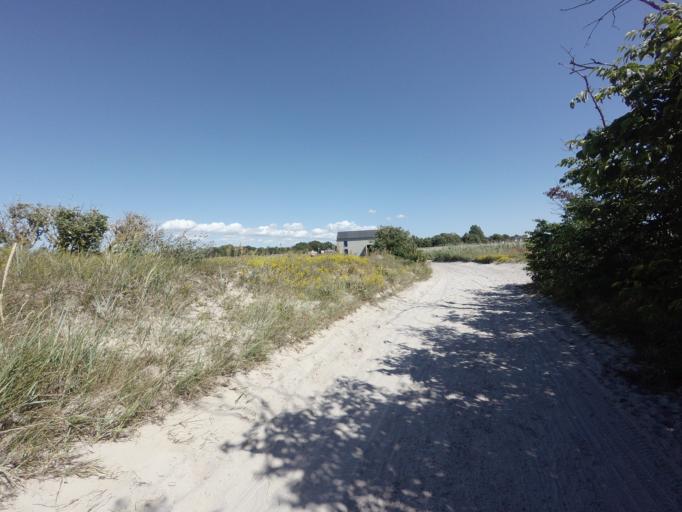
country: SE
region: Skane
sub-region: Vellinge Kommun
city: Skanor med Falsterbo
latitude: 55.3941
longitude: 12.8227
